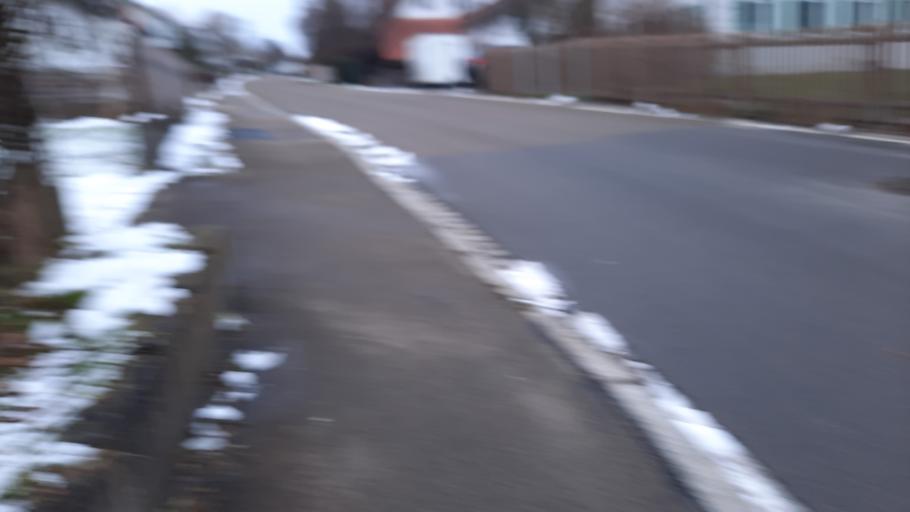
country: DE
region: Bavaria
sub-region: Swabia
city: Memmingen
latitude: 47.9541
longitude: 10.1742
